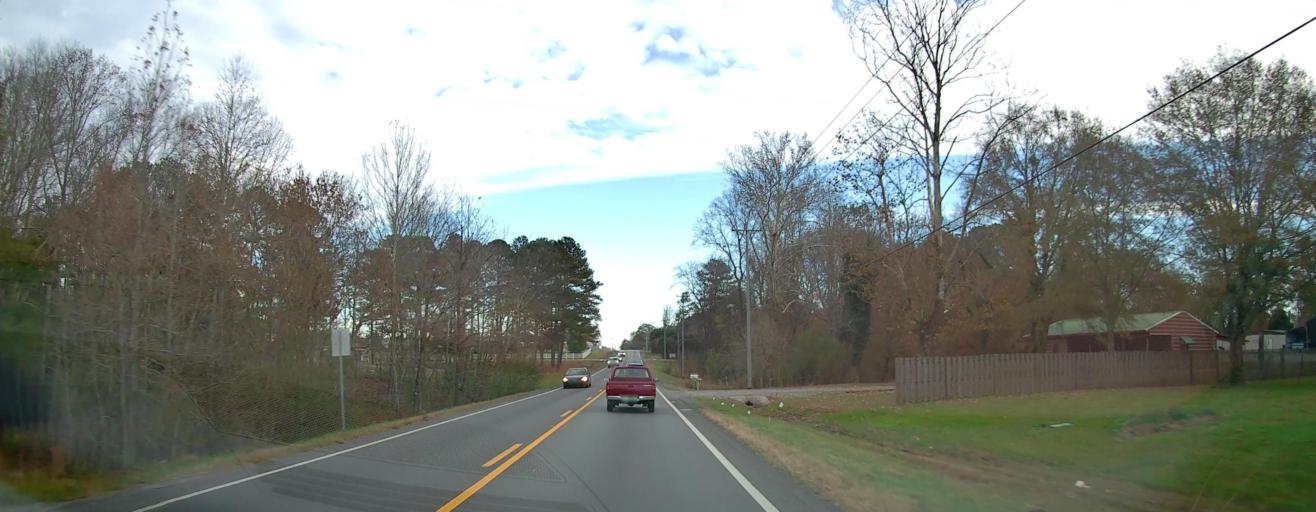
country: US
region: Alabama
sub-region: Morgan County
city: Priceville
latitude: 34.4753
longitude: -86.8102
